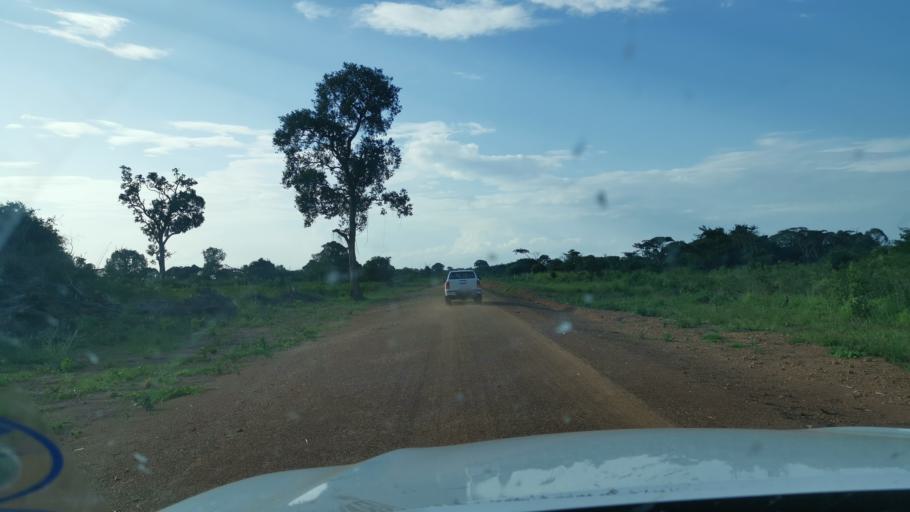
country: ZM
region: Luapula
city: Samfya
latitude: -11.1162
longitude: 29.5786
